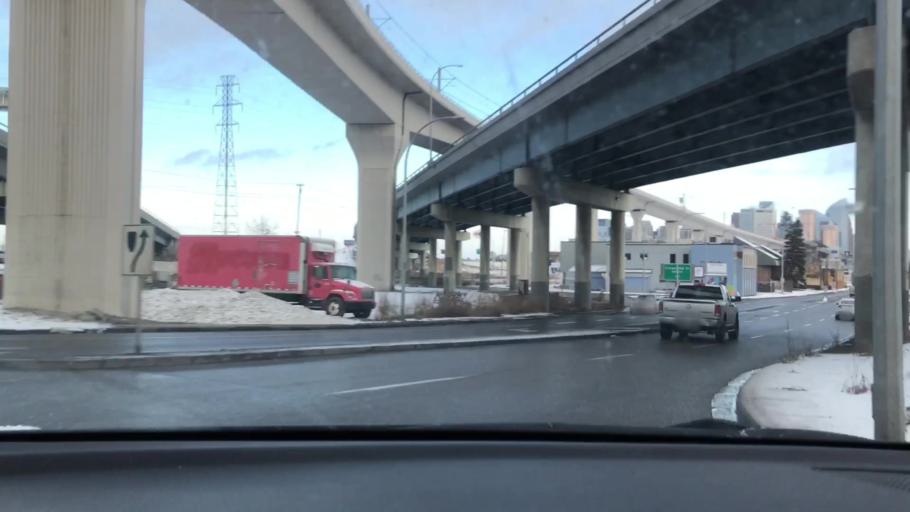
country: CA
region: Alberta
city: Calgary
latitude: 51.0446
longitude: -114.1085
